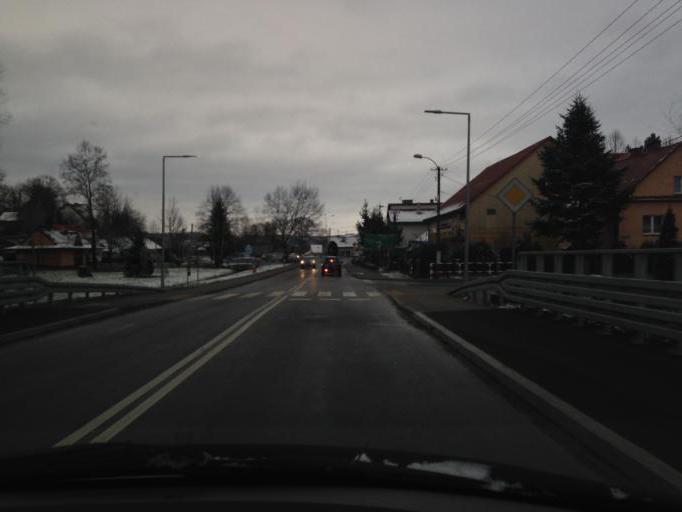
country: PL
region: Lesser Poland Voivodeship
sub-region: Powiat tarnowski
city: Gromnik
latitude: 49.8386
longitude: 20.9587
